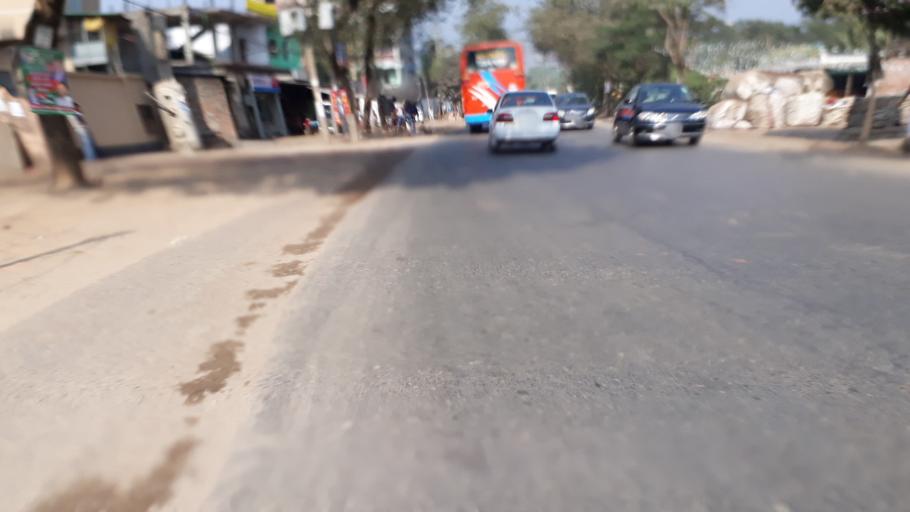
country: BD
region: Dhaka
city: Tungi
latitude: 23.9087
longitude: 90.3203
